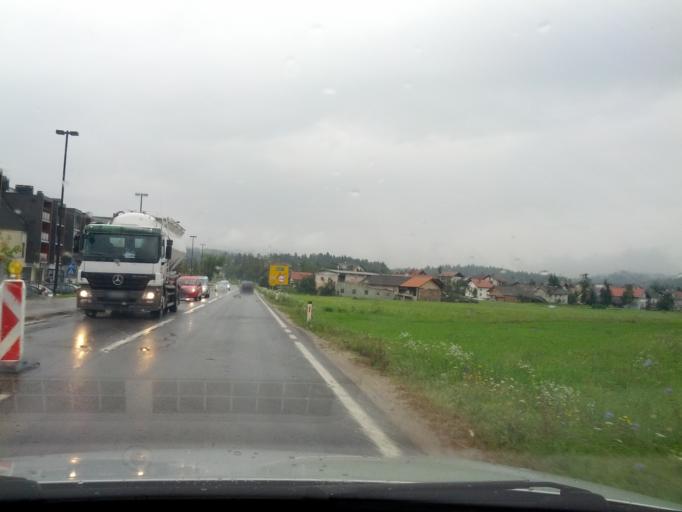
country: SI
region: Logatec
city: Logatec
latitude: 45.9127
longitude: 14.2251
